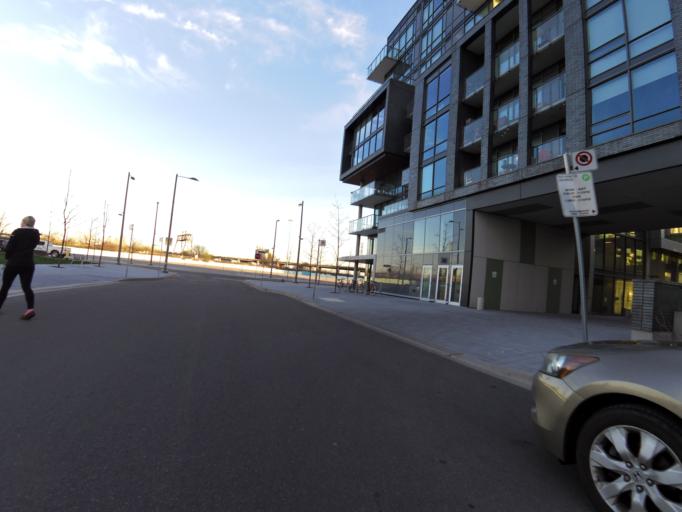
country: CA
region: Ontario
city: Toronto
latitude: 43.6523
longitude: -79.3555
